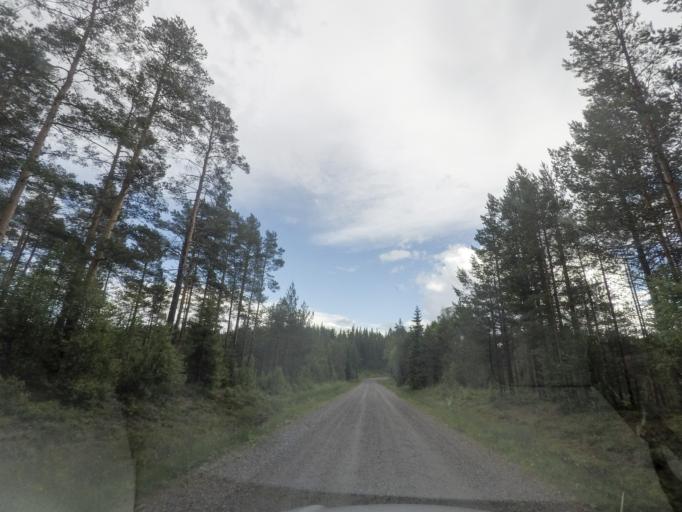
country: SE
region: OErebro
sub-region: Hallefors Kommun
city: Haellefors
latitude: 60.0229
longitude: 14.5636
